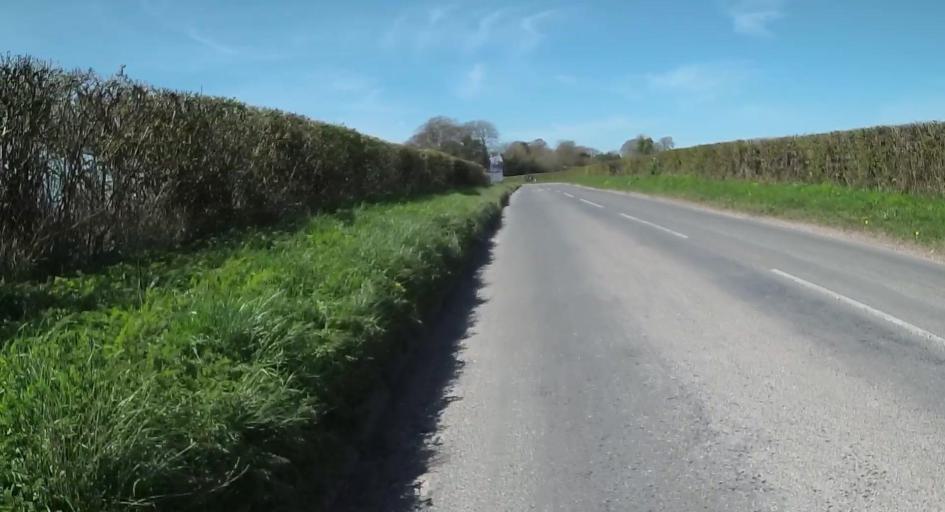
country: GB
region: England
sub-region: Hampshire
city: Winchester
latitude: 51.0984
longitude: -1.3595
